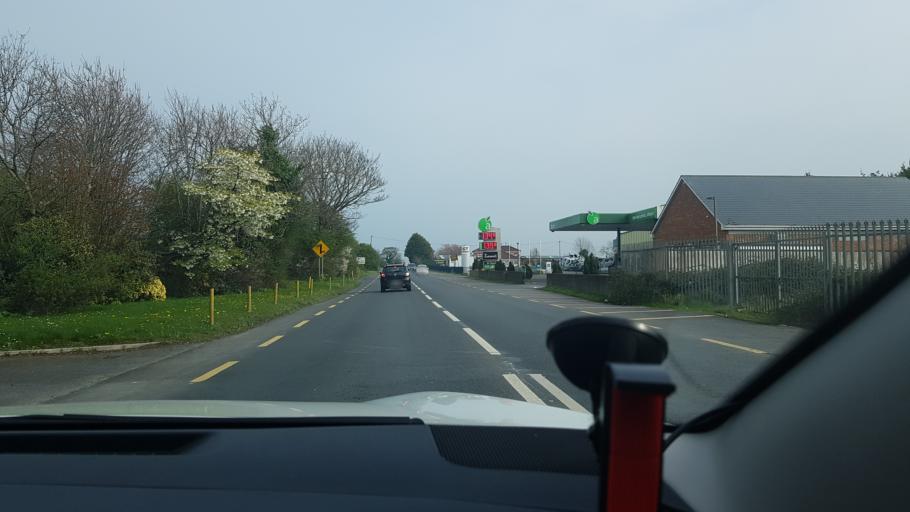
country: IE
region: Leinster
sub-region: An Mhi
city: Stamullin
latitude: 53.6603
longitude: -6.2681
